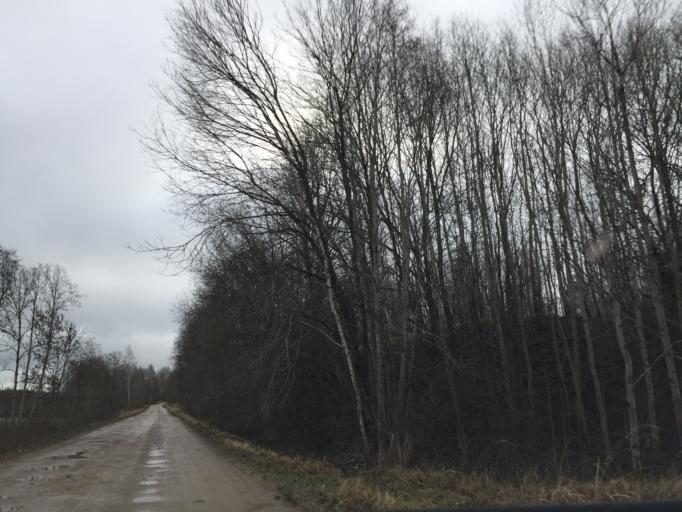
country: LV
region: Broceni
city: Broceni
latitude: 56.6619
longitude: 22.5532
